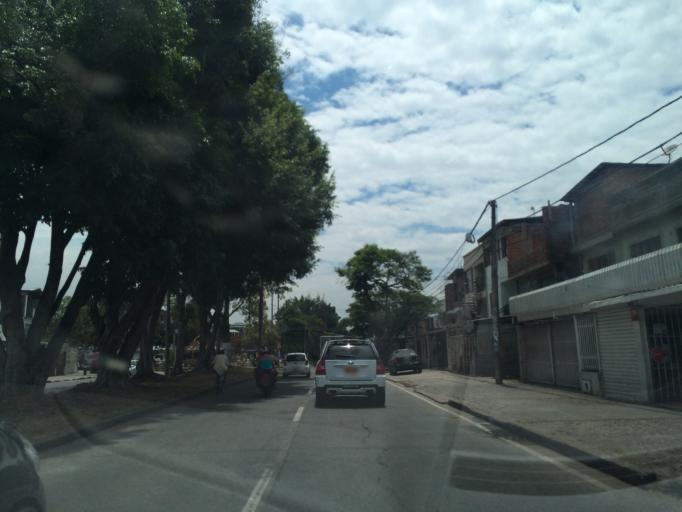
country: CO
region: Valle del Cauca
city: Cali
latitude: 3.4111
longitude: -76.5255
